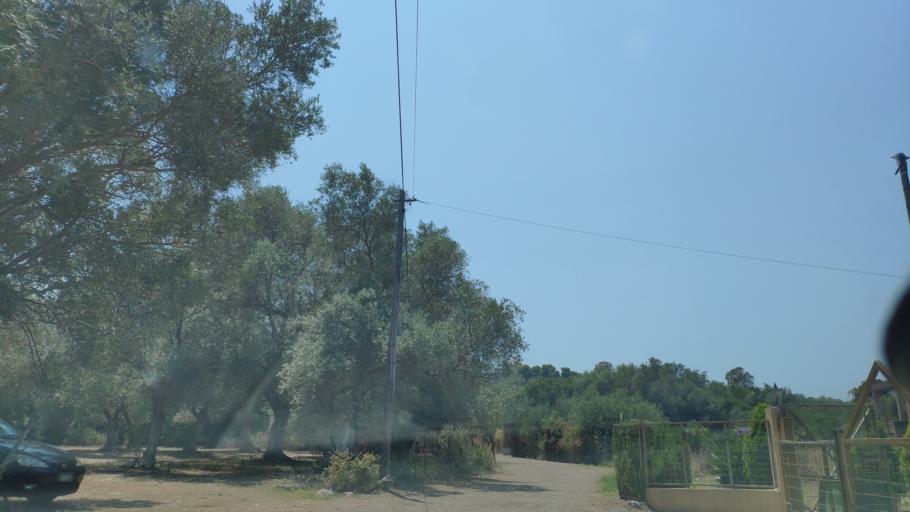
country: GR
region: West Greece
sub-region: Nomos Aitolias kai Akarnanias
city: Amfilochia
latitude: 38.9046
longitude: 21.1210
